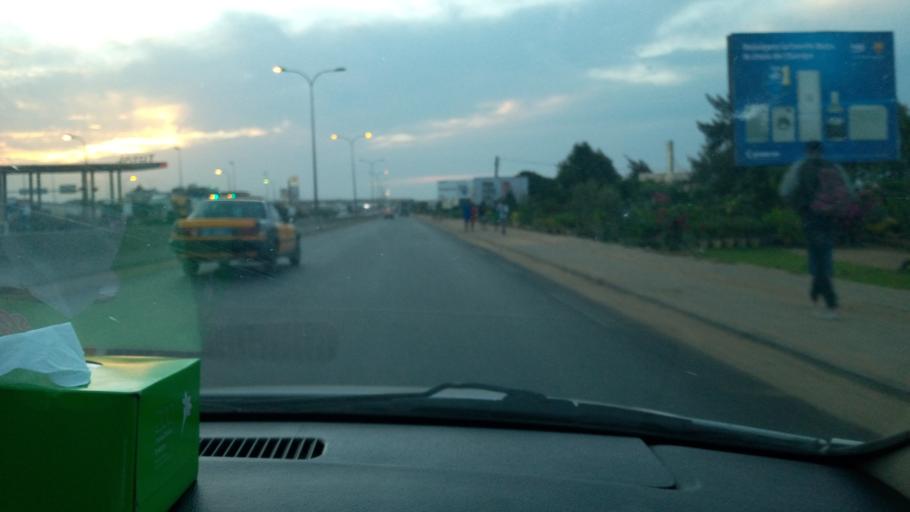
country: SN
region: Dakar
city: Pikine
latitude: 14.7467
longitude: -17.4108
